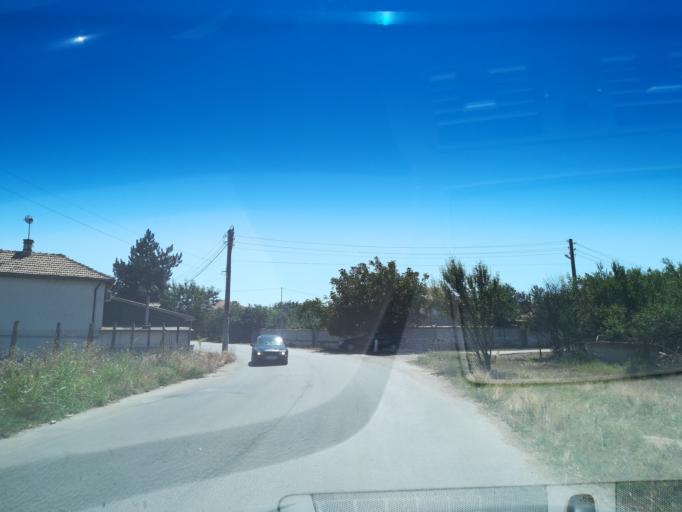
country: BG
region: Pazardzhik
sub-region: Obshtina Pazardzhik
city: Pazardzhik
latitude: 42.3408
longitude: 24.4001
